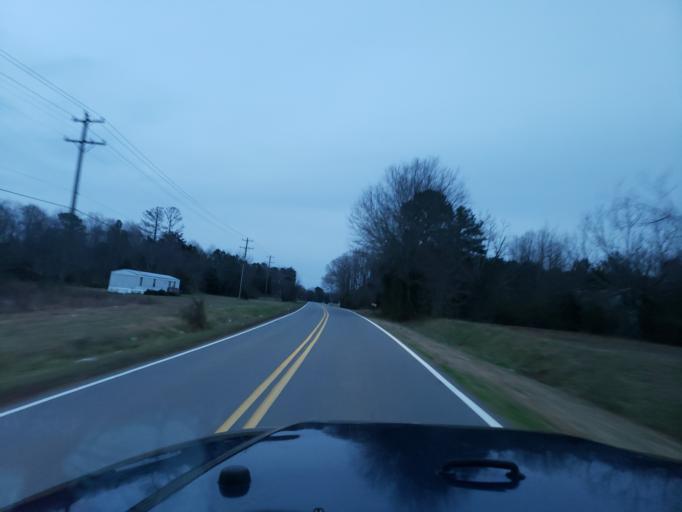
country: US
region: North Carolina
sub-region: Cleveland County
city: White Plains
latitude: 35.1915
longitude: -81.4387
